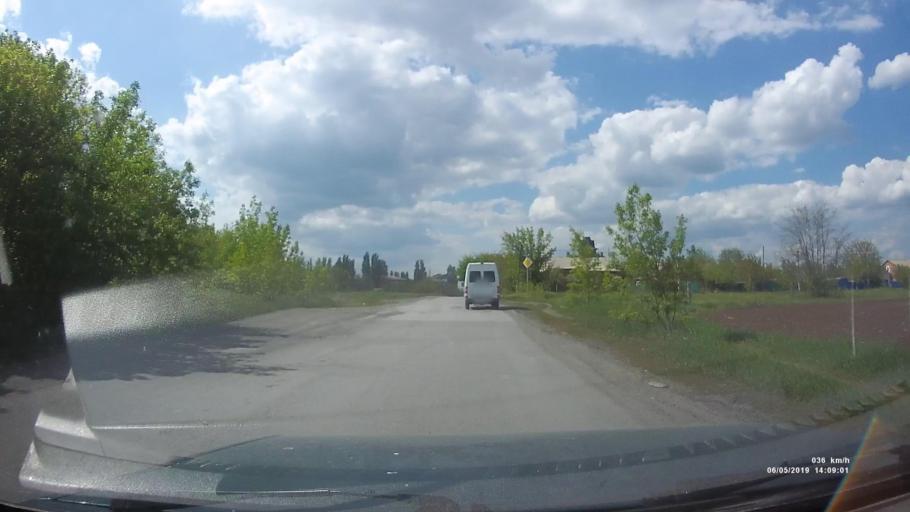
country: RU
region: Rostov
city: Shakhty
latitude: 47.6852
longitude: 40.2935
